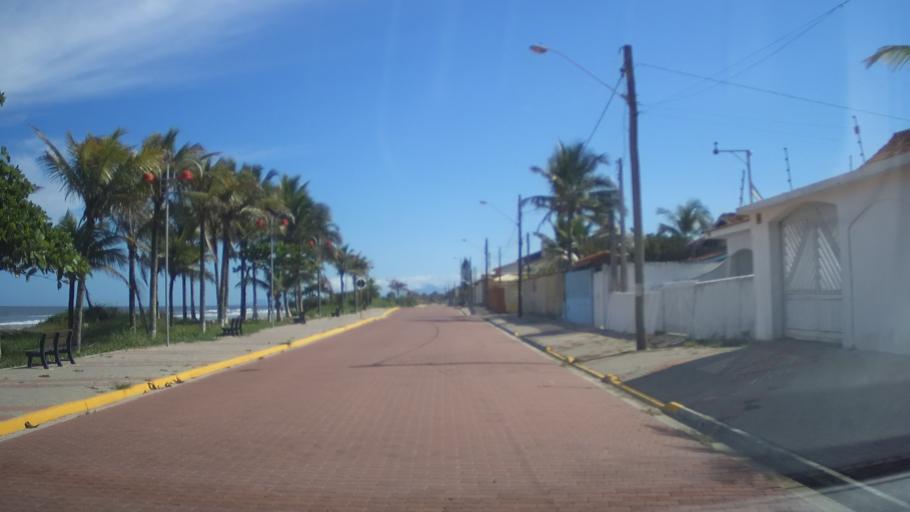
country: BR
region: Sao Paulo
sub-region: Itanhaem
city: Itanhaem
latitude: -24.1675
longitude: -46.7532
